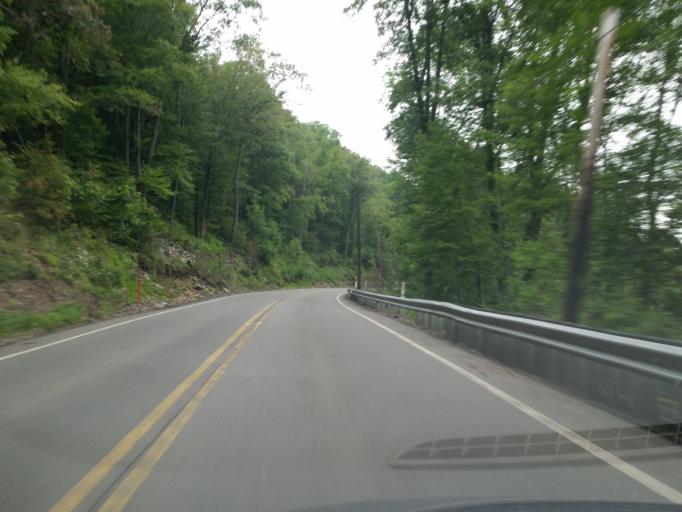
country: US
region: Pennsylvania
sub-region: Schuylkill County
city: Valley View
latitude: 40.6078
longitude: -76.4863
